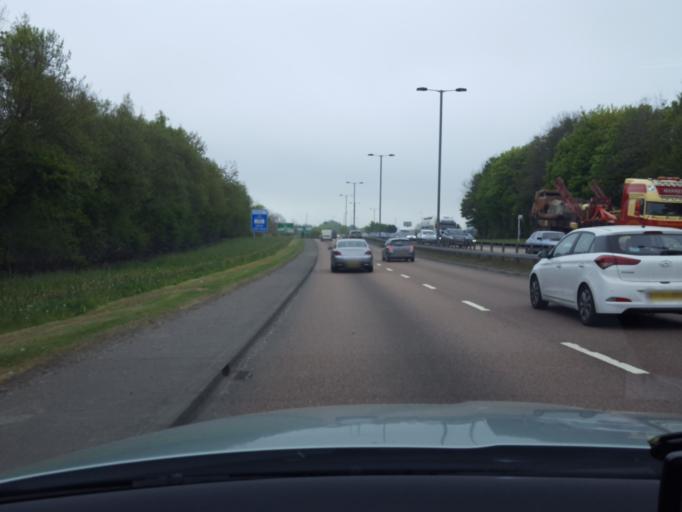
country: GB
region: Scotland
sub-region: Dundee City
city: Dundee
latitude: 56.4919
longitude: -2.9507
